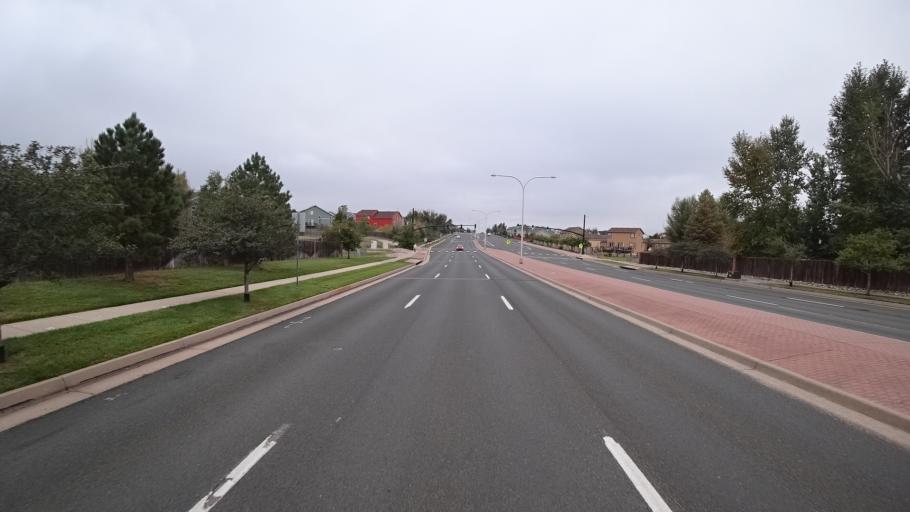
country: US
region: Colorado
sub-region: El Paso County
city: Cimarron Hills
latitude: 38.9065
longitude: -104.6965
